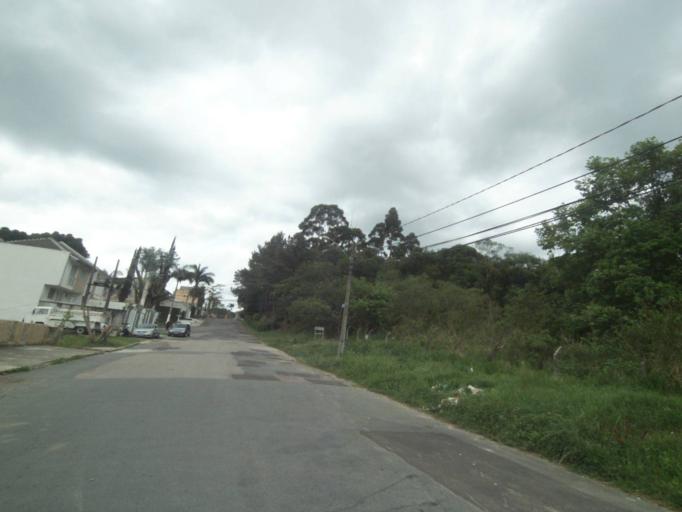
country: BR
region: Parana
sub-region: Curitiba
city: Curitiba
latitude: -25.3878
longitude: -49.2841
